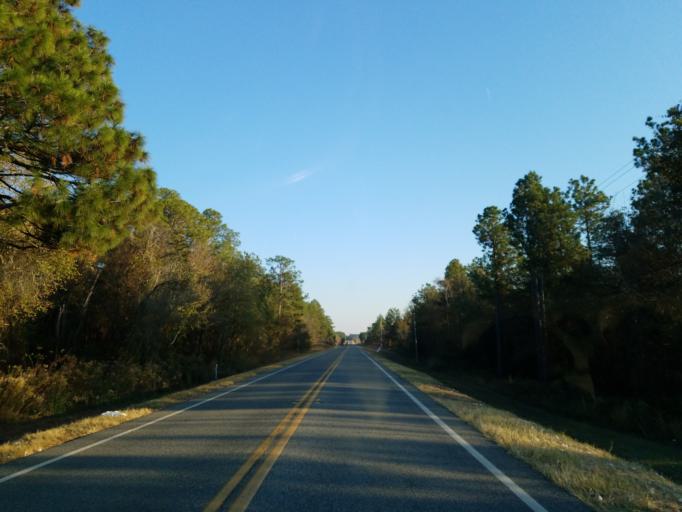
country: US
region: Georgia
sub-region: Crisp County
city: Cordele
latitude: 31.8882
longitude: -83.6827
